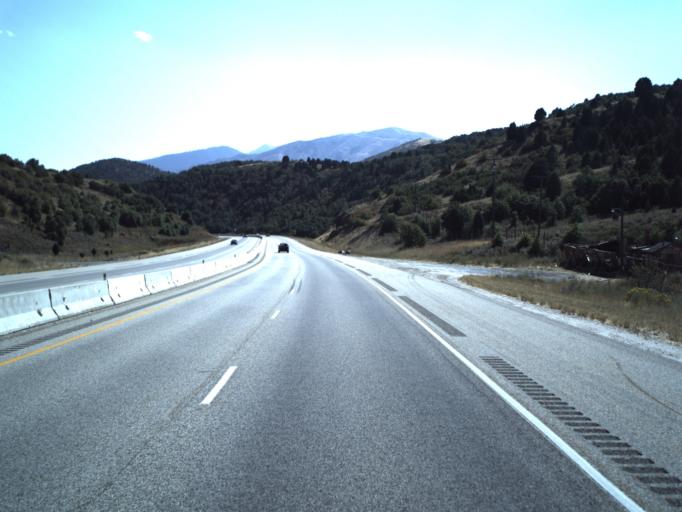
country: US
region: Utah
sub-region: Box Elder County
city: Brigham City
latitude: 41.5386
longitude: -111.9581
